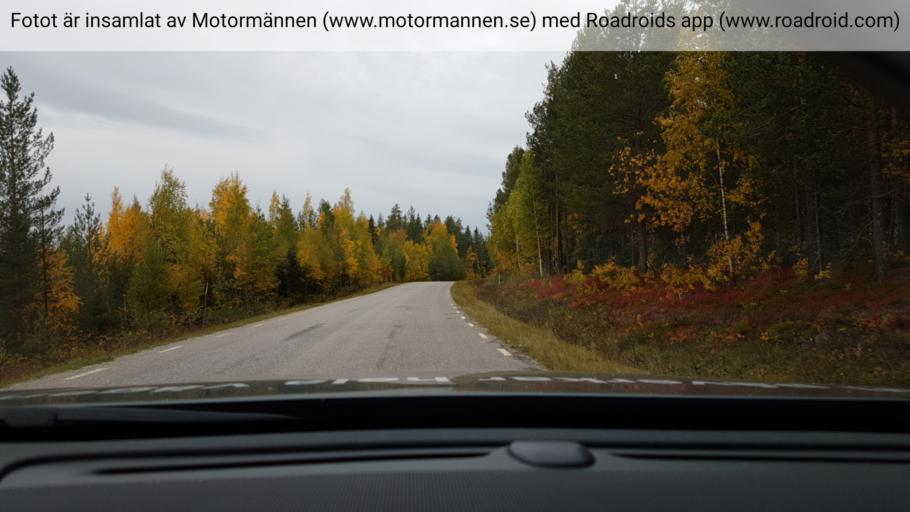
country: SE
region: Norrbotten
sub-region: Overkalix Kommun
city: OEverkalix
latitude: 66.2318
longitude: 22.9932
